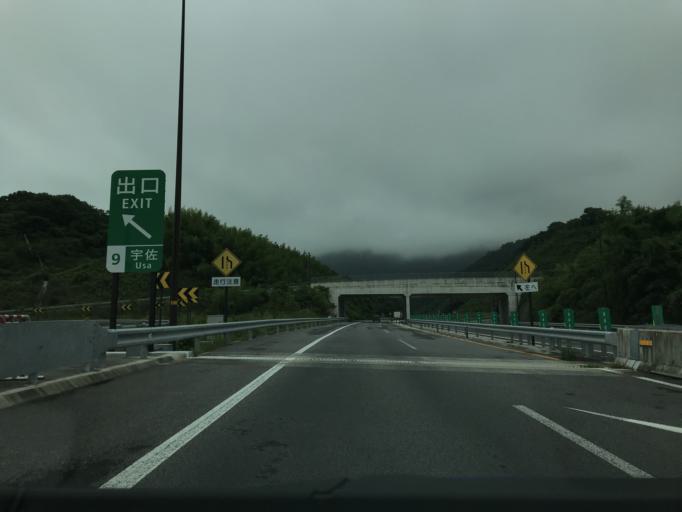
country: JP
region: Oita
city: Bungo-Takada-shi
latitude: 33.4988
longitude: 131.3169
